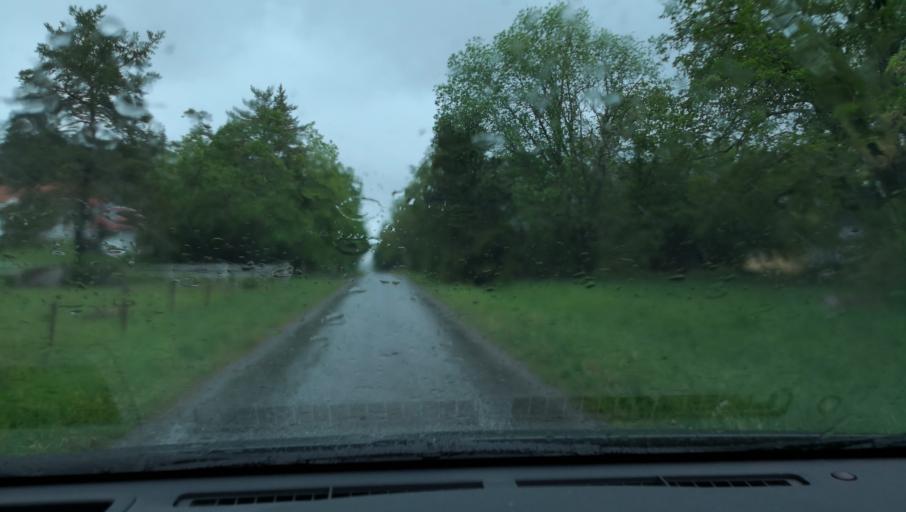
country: SE
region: Uppsala
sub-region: Enkopings Kommun
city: Orsundsbro
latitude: 59.7716
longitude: 17.3442
